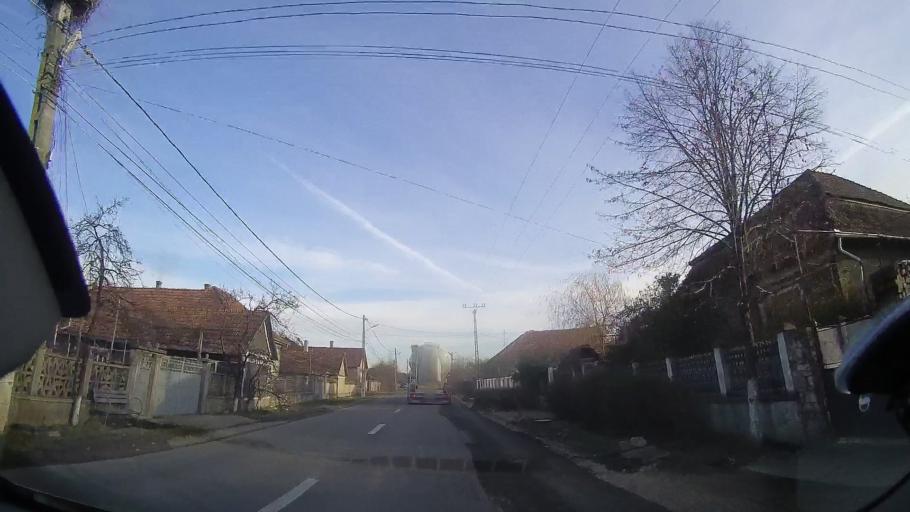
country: RO
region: Bihor
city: Lugasu de Jos
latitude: 47.0420
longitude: 22.3584
